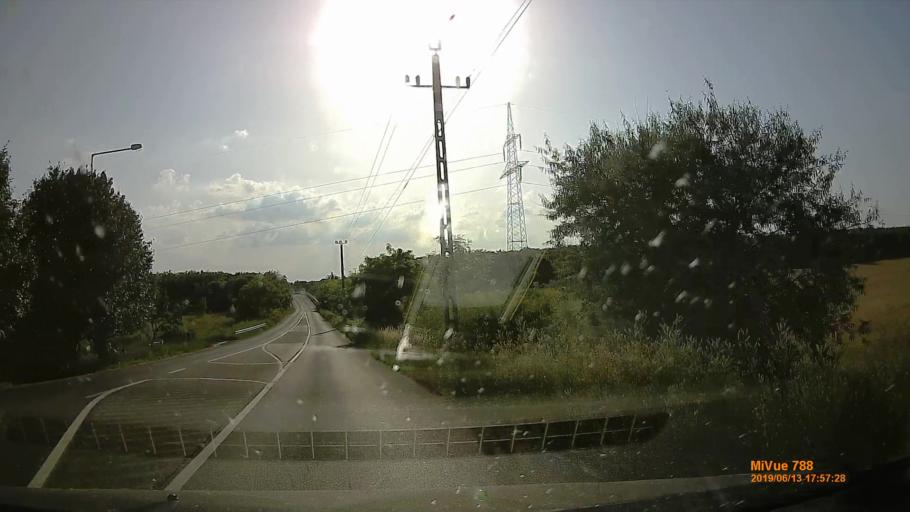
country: HU
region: Pest
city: Ecser
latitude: 47.4458
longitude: 19.3361
